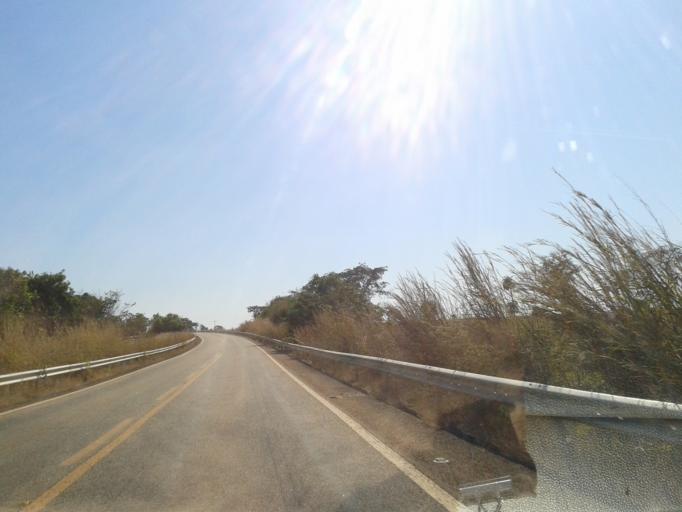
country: BR
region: Goias
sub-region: Mozarlandia
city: Mozarlandia
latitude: -14.3101
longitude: -50.4054
